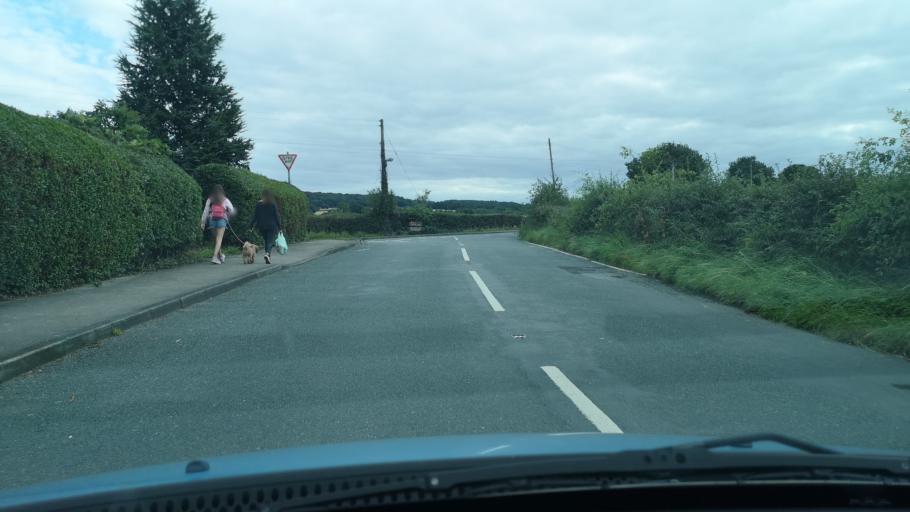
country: GB
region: England
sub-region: City and Borough of Wakefield
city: Crigglestone
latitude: 53.6347
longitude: -1.5459
